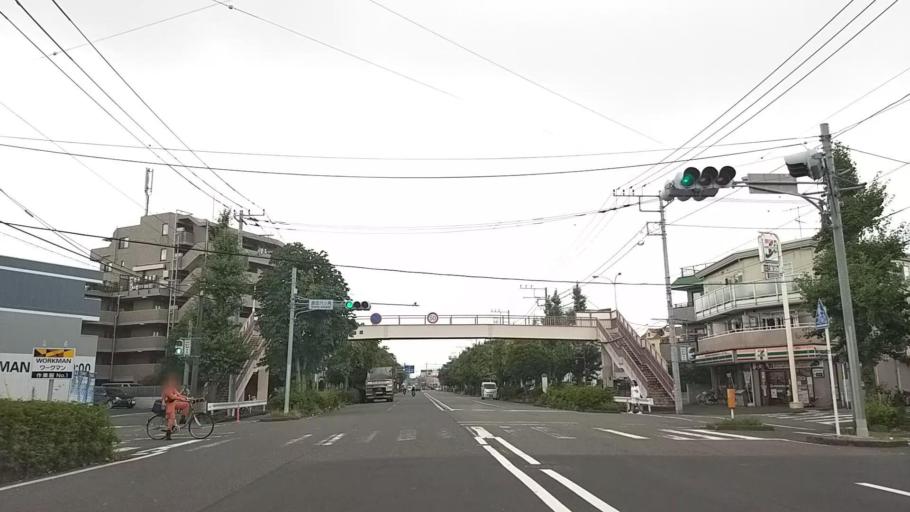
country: JP
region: Kanagawa
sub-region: Kawasaki-shi
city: Kawasaki
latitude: 35.5184
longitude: 139.7097
